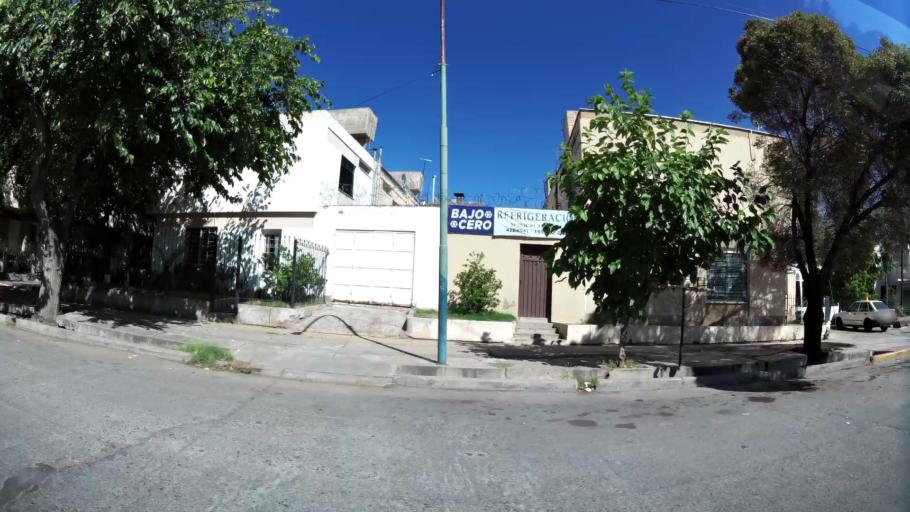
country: AR
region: Mendoza
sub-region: Departamento de Godoy Cruz
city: Godoy Cruz
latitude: -32.9078
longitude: -68.8741
